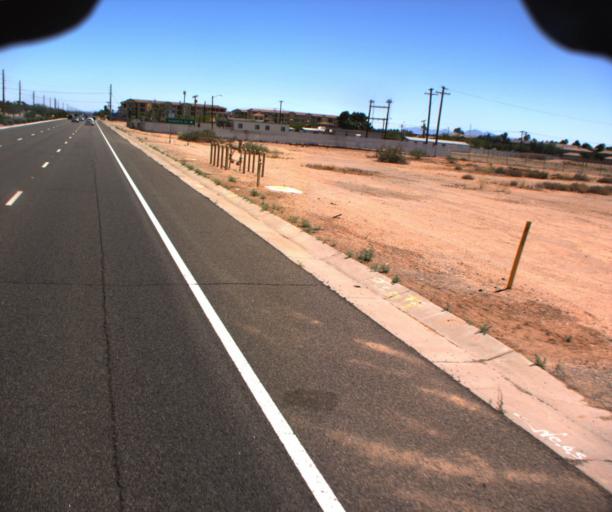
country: US
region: Arizona
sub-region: Maricopa County
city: Sun City West
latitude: 33.6627
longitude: -112.3813
